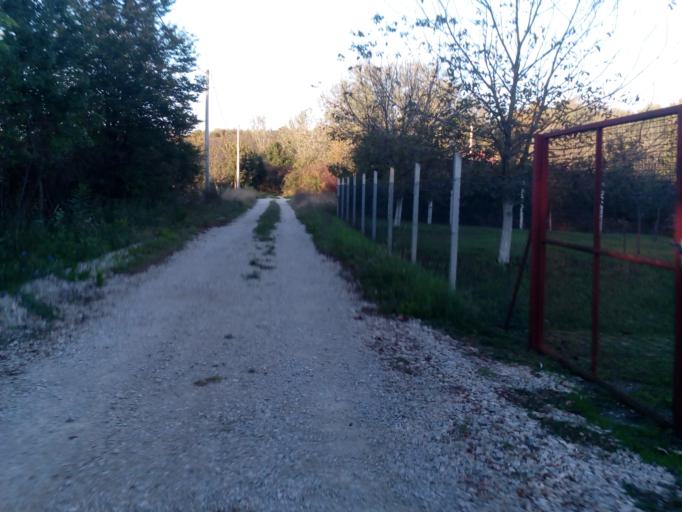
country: HR
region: Vukovarsko-Srijemska
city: Mirkovci
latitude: 45.2387
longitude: 18.8272
